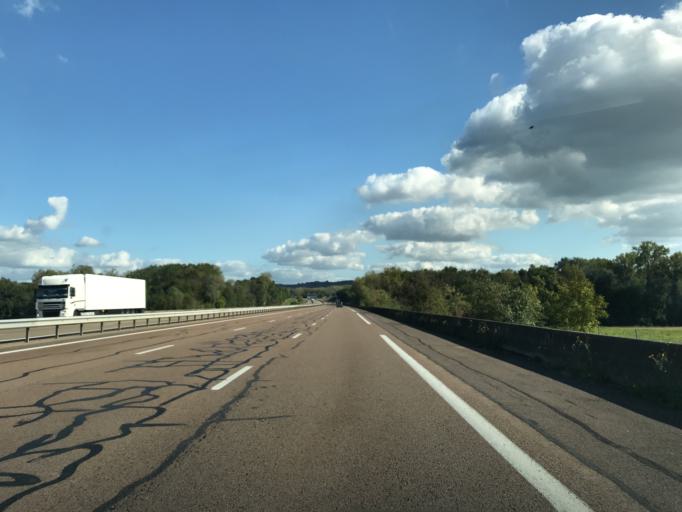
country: FR
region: Bourgogne
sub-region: Departement de l'Yonne
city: Fleury-la-Vallee
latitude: 47.8871
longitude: 3.4198
